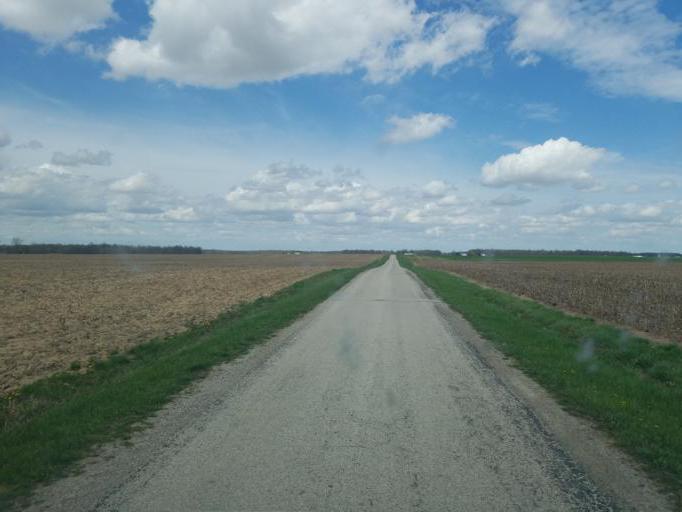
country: US
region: Ohio
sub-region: Crawford County
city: Bucyrus
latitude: 40.8723
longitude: -82.9880
